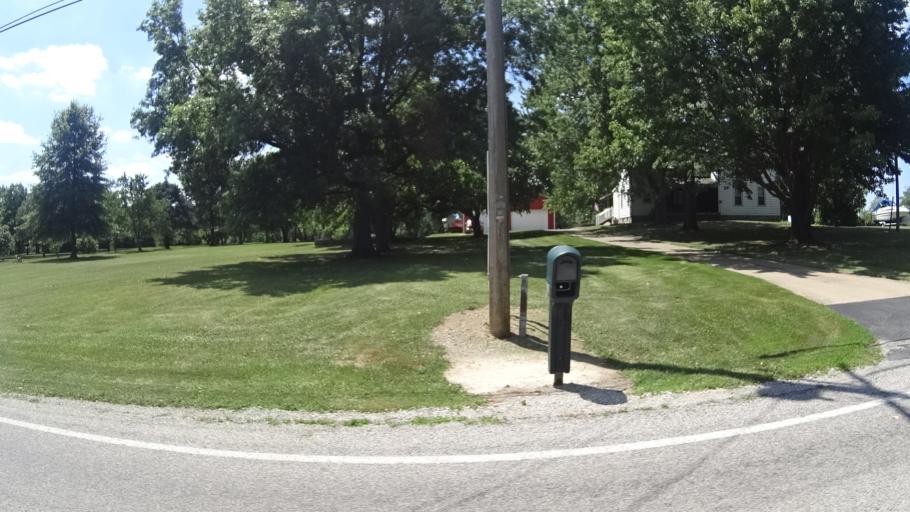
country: US
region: Ohio
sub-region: Erie County
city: Huron
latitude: 41.4009
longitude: -82.6116
